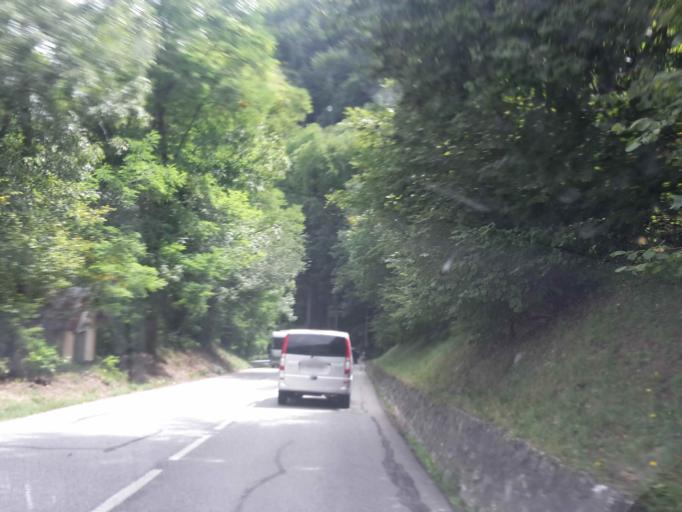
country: FR
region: Rhone-Alpes
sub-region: Departement de la Savoie
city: Saint-Michel-de-Maurienne
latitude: 45.2076
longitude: 6.4583
